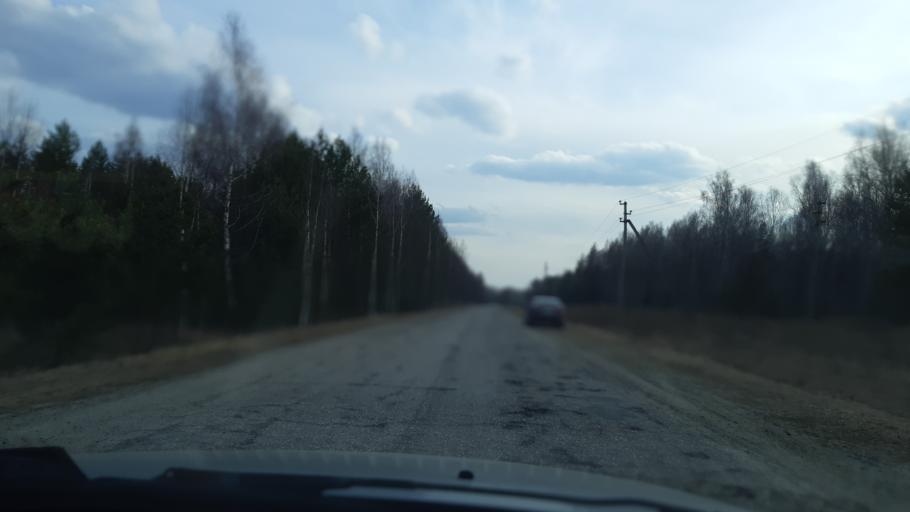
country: RU
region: Vladimir
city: Nikologory
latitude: 56.1142
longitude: 41.9845
